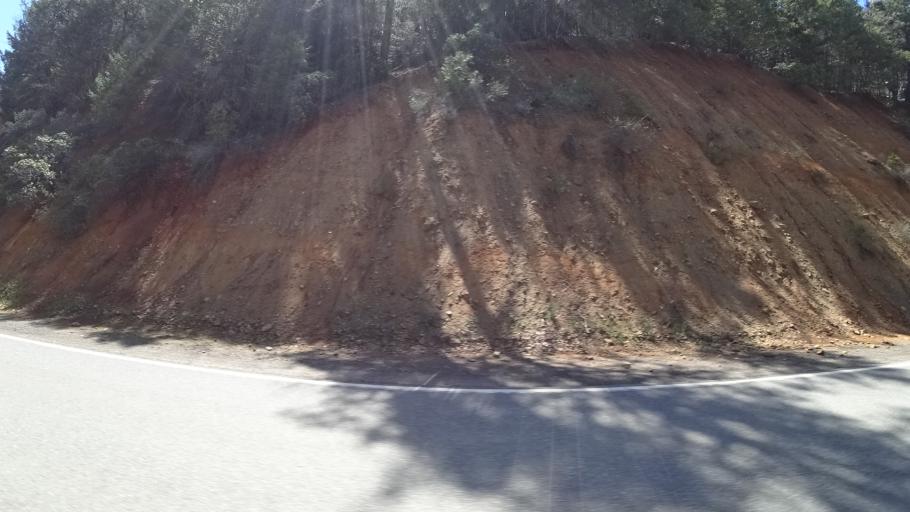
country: US
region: California
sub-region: Trinity County
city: Weaverville
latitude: 40.8004
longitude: -122.8894
